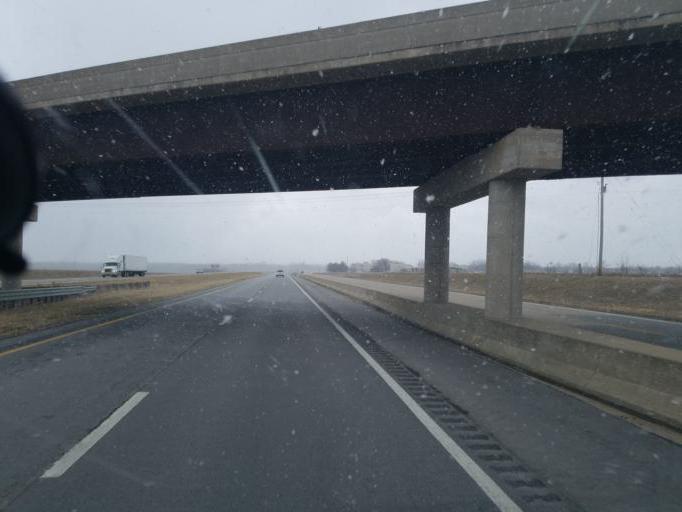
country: US
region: Missouri
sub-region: Randolph County
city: Moberly
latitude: 39.4313
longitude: -92.4160
